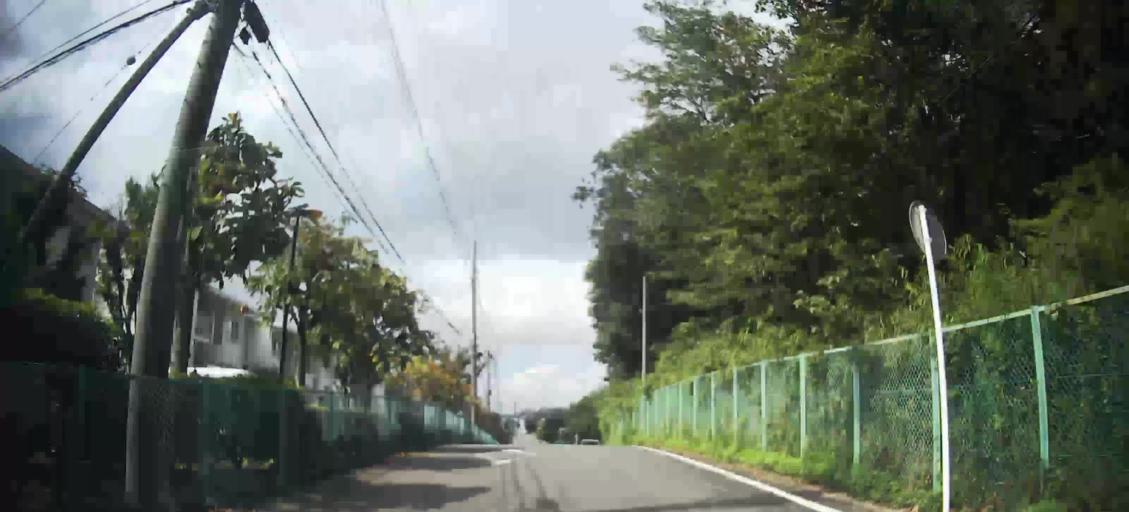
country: JP
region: Kanagawa
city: Yokohama
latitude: 35.4820
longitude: 139.5539
